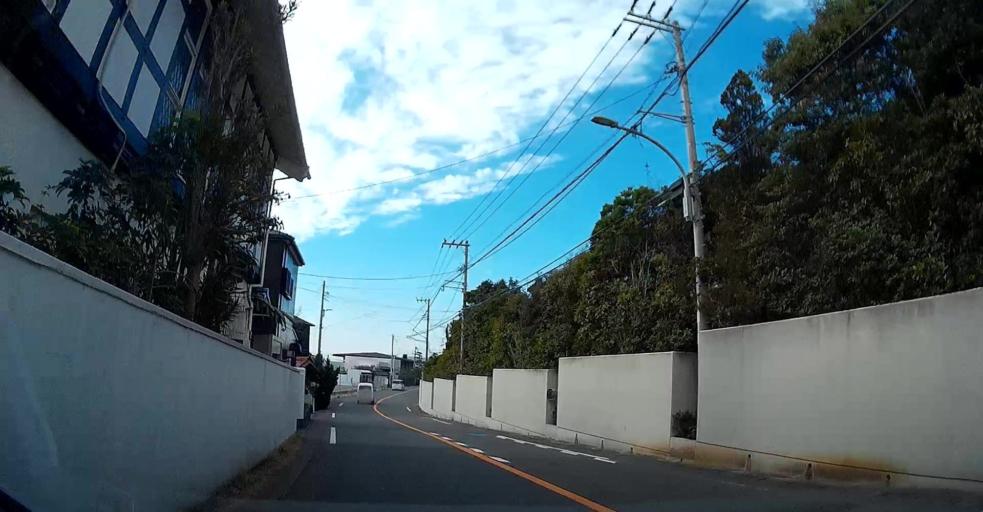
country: JP
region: Kanagawa
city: Hayama
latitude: 35.2658
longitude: 139.5748
